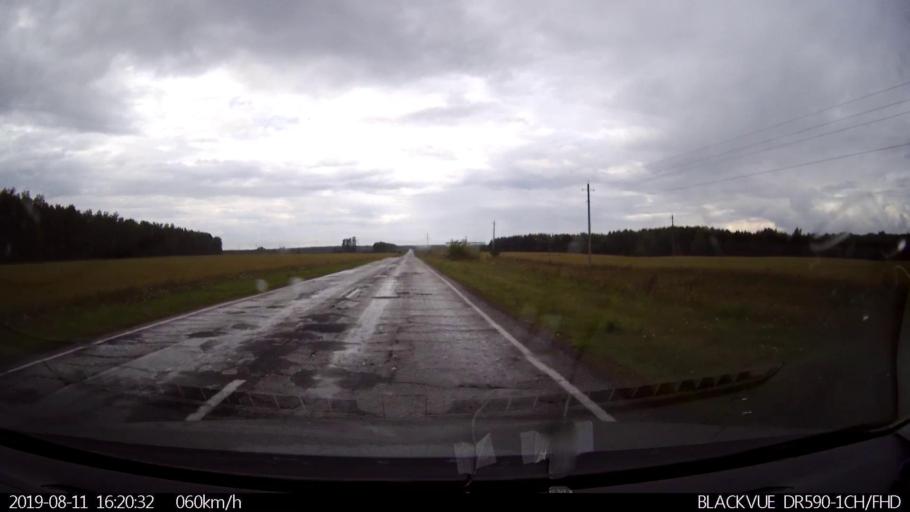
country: RU
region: Ulyanovsk
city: Mayna
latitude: 54.0726
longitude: 47.6024
